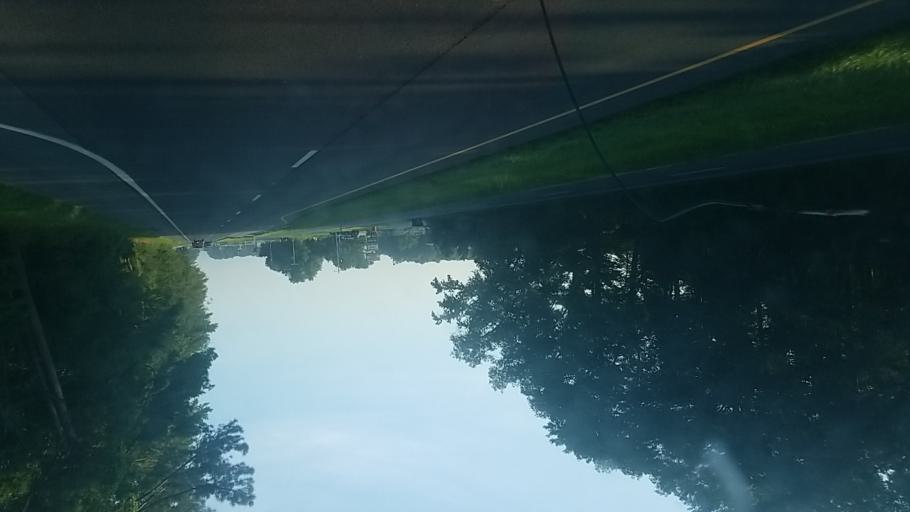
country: US
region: Delaware
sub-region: Sussex County
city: Selbyville
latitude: 38.4852
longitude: -75.2359
